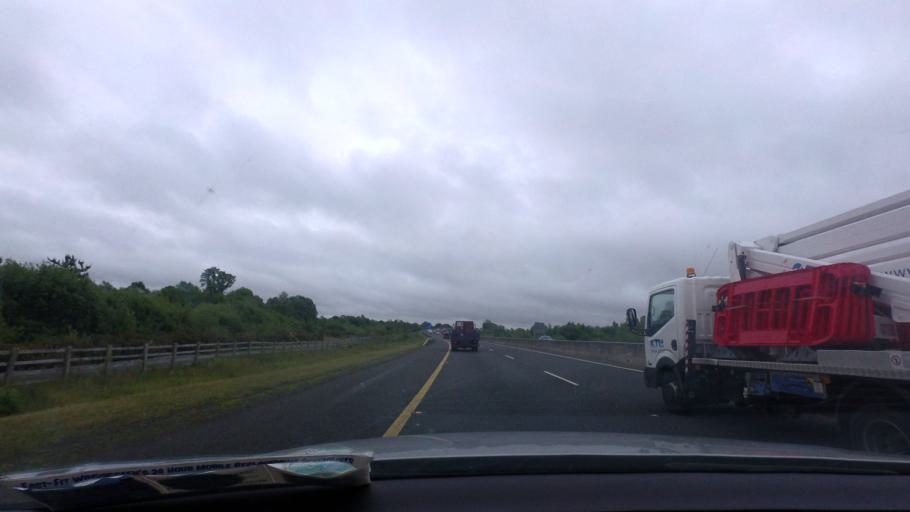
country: IE
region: Munster
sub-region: County Limerick
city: Castleconnell
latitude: 52.6904
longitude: -8.4986
